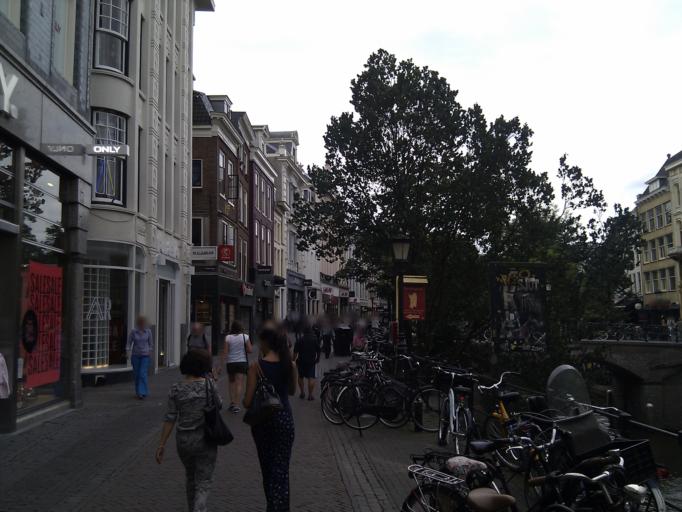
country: NL
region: Utrecht
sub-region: Gemeente Utrecht
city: Utrecht
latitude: 52.0916
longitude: 5.1191
